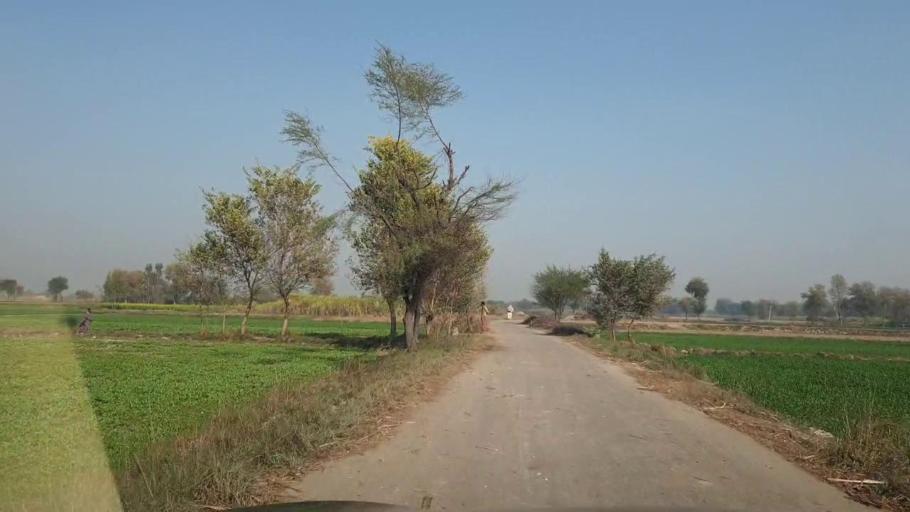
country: PK
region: Sindh
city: Ubauro
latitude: 28.1304
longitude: 69.7667
